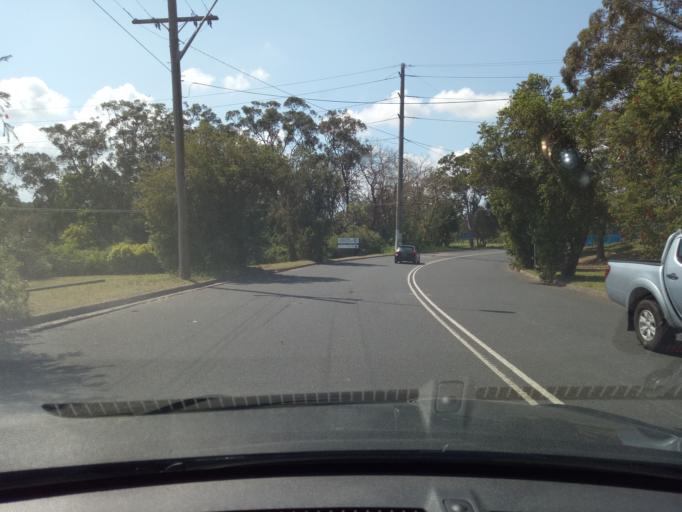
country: AU
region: New South Wales
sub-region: Gosford Shire
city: Gosford
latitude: -33.4196
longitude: 151.3305
